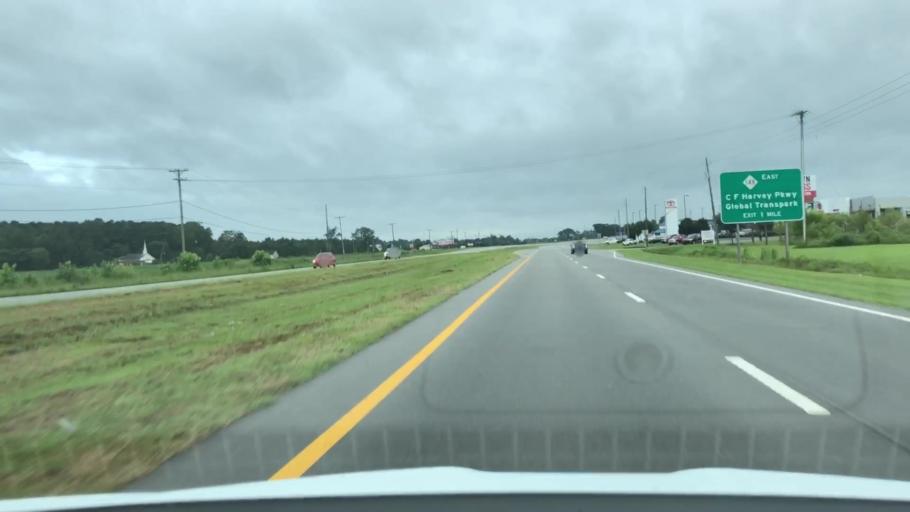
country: US
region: North Carolina
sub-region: Lenoir County
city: Kinston
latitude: 35.2604
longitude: -77.6579
